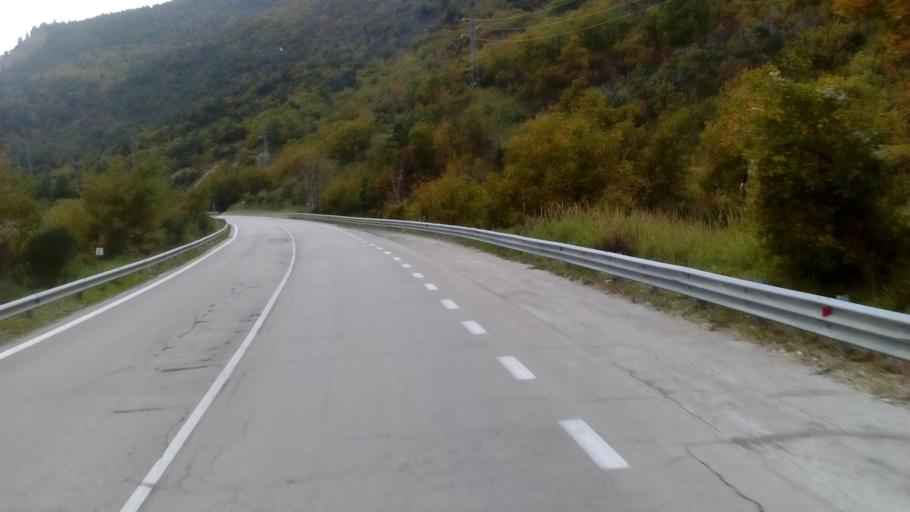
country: IT
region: Molise
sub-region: Provincia di Campobasso
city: Roccavivara
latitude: 41.8473
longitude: 14.5885
